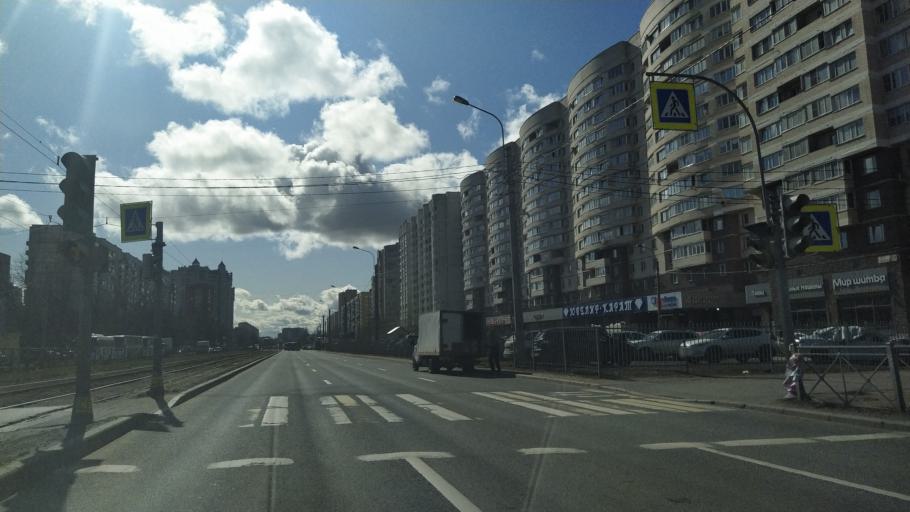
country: RU
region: St.-Petersburg
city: Ozerki
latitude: 60.0498
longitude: 30.3324
